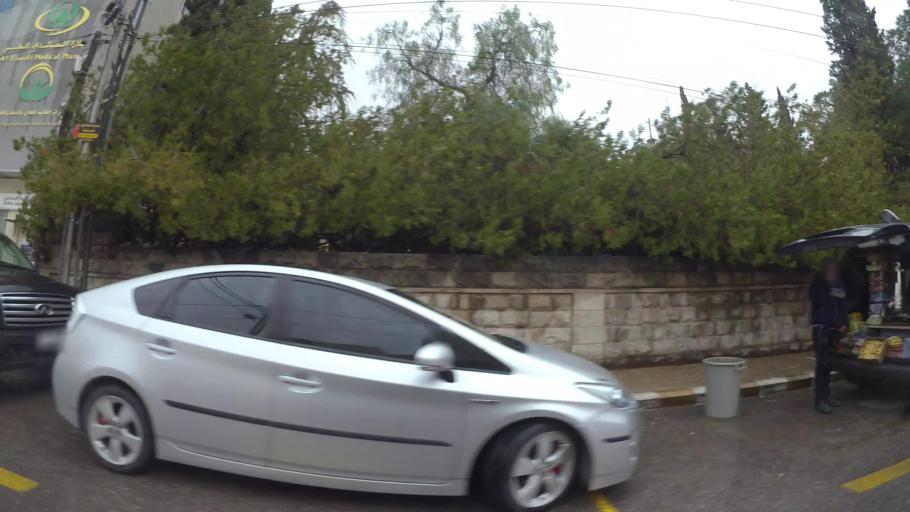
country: JO
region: Amman
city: Amman
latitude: 31.9509
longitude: 35.9042
